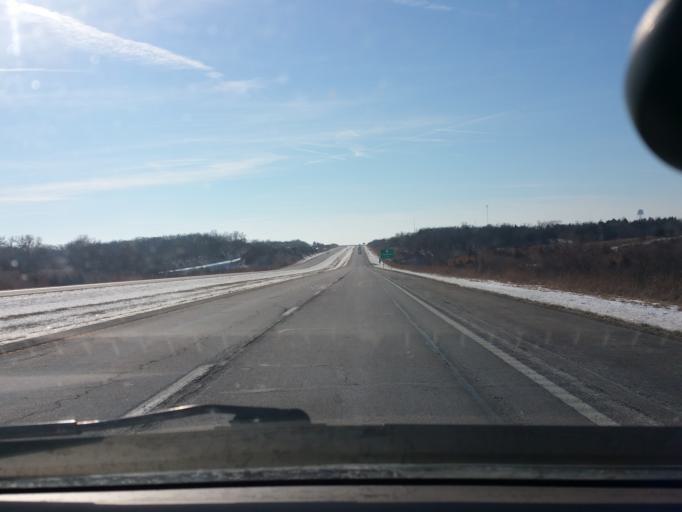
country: US
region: Missouri
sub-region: Harrison County
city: Bethany
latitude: 40.3934
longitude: -93.9978
